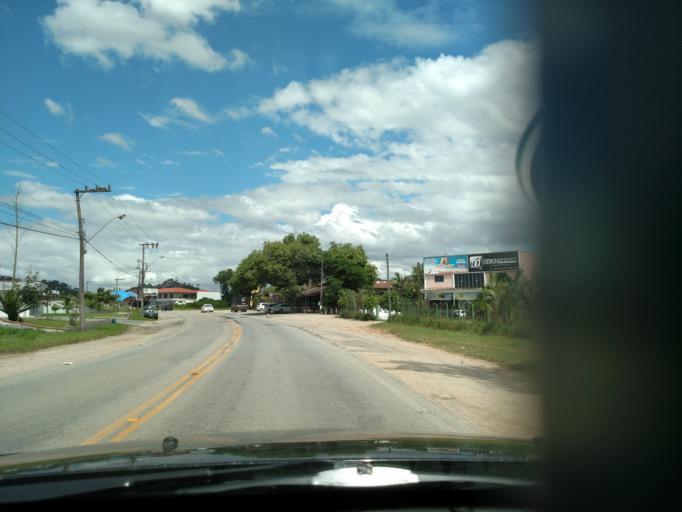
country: BR
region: Santa Catarina
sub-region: Gaspar
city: Gaspar
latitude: -26.9267
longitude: -48.8937
